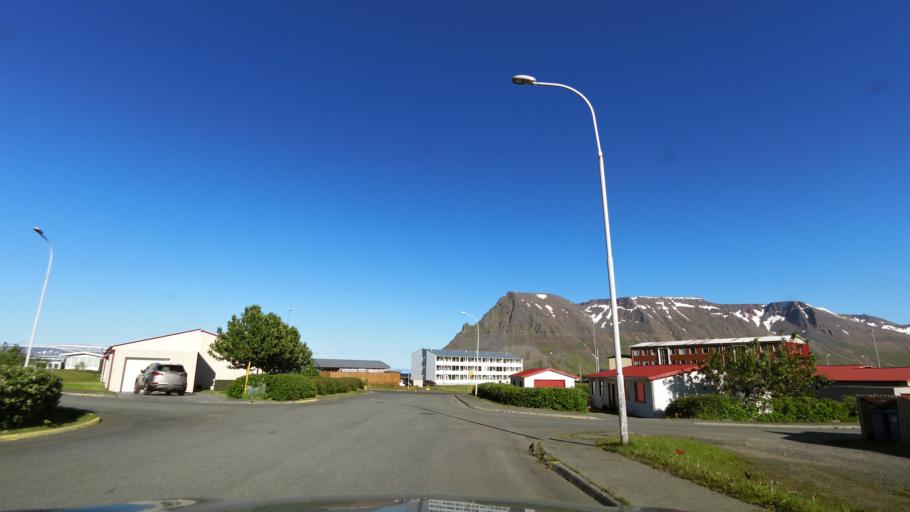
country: IS
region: Westfjords
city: Isafjoerdur
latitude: 66.1600
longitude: -23.2636
